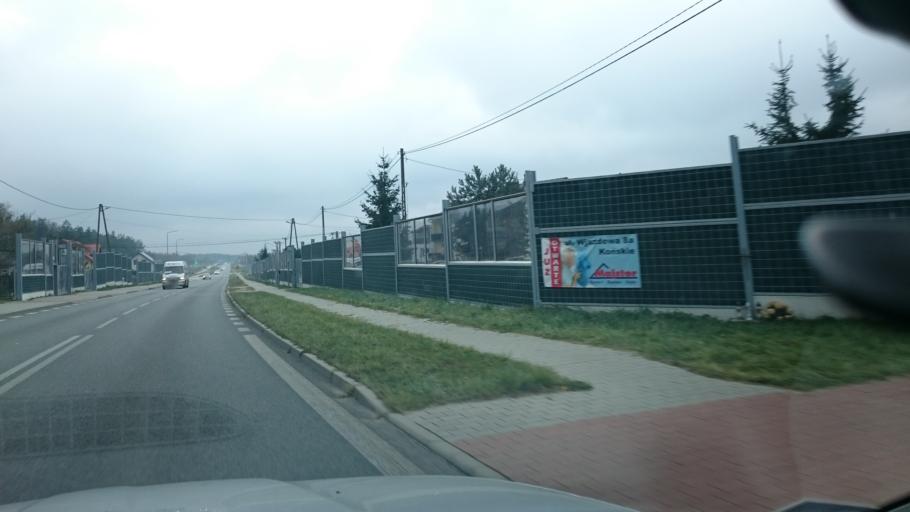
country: PL
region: Swietokrzyskie
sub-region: Powiat konecki
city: Konskie
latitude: 51.1407
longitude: 20.3645
